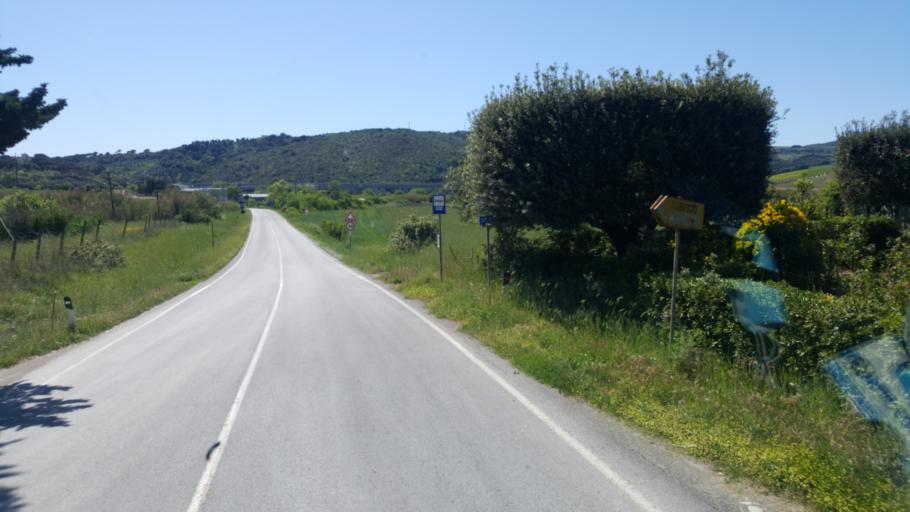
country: IT
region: Tuscany
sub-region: Provincia di Livorno
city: Rosignano Marittimo
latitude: 43.4117
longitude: 10.5034
